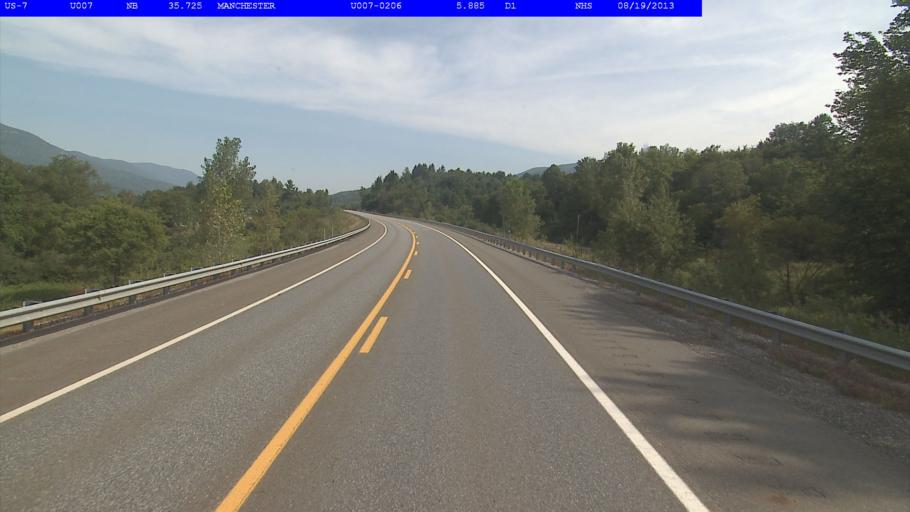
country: US
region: Vermont
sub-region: Bennington County
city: Manchester Center
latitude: 43.1872
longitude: -73.0155
